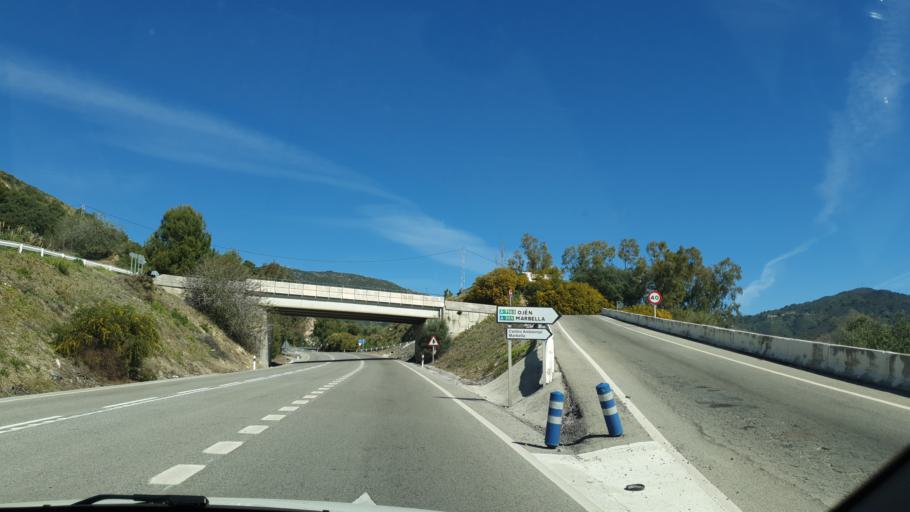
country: ES
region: Andalusia
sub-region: Provincia de Malaga
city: Ojen
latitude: 36.5474
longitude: -4.8613
